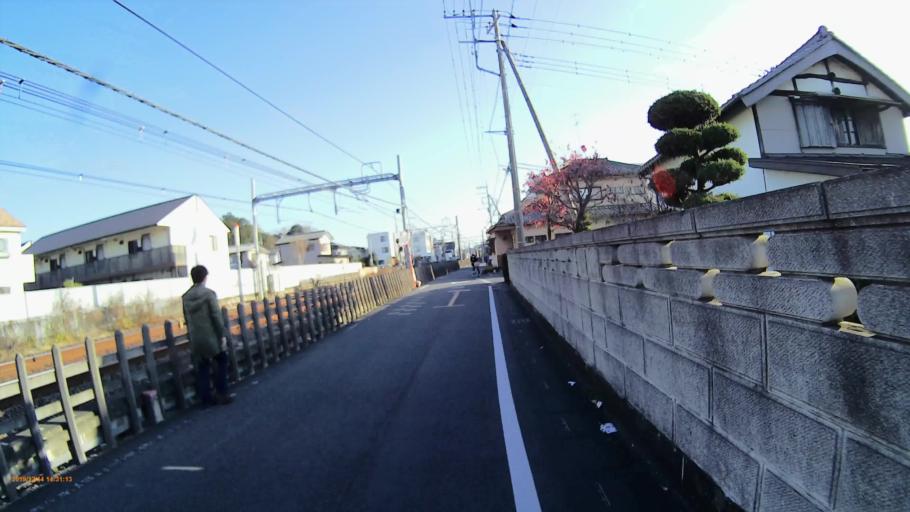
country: JP
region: Saitama
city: Konosu
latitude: 36.0365
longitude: 139.5306
